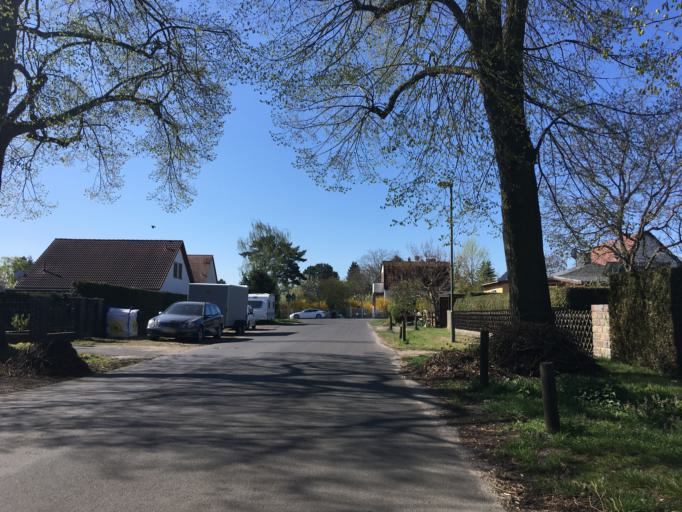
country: DE
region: Berlin
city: Buchholz
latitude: 52.6006
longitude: 13.4256
